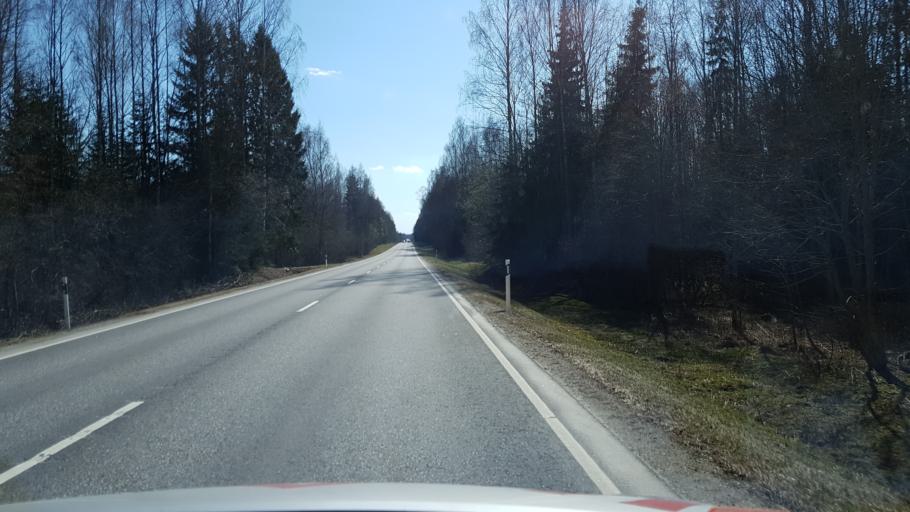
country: EE
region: Jogevamaa
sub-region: Mustvee linn
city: Mustvee
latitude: 58.6949
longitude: 26.8140
